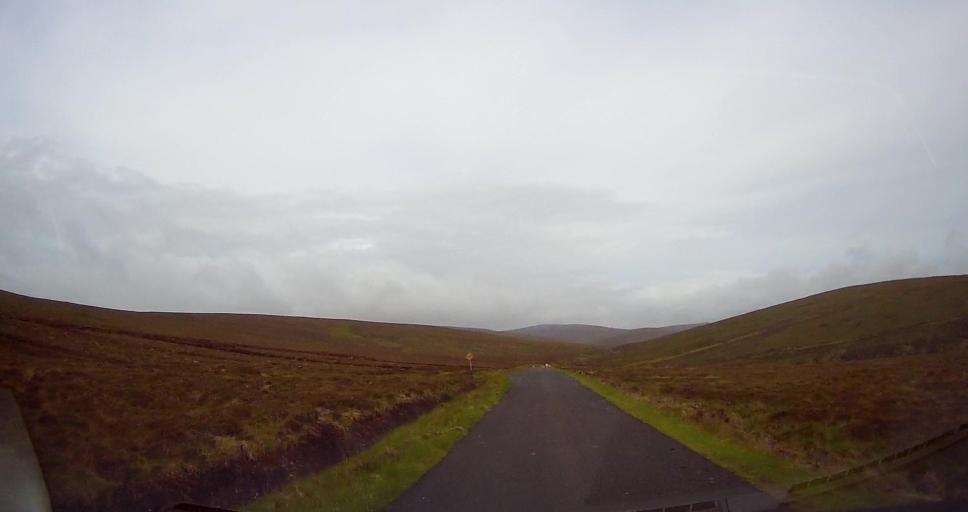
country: GB
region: Scotland
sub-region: Orkney Islands
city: Stromness
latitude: 58.8583
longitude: -3.2201
